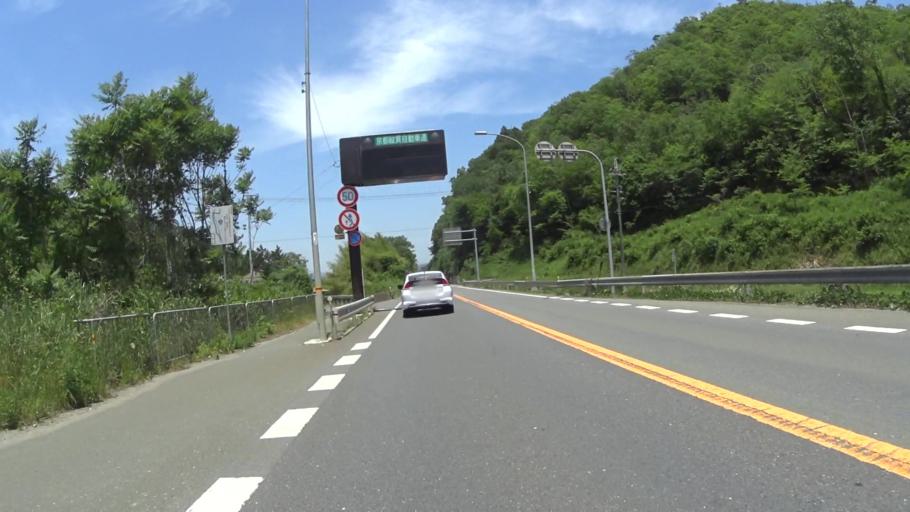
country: JP
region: Kyoto
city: Kameoka
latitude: 35.1433
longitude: 135.4267
